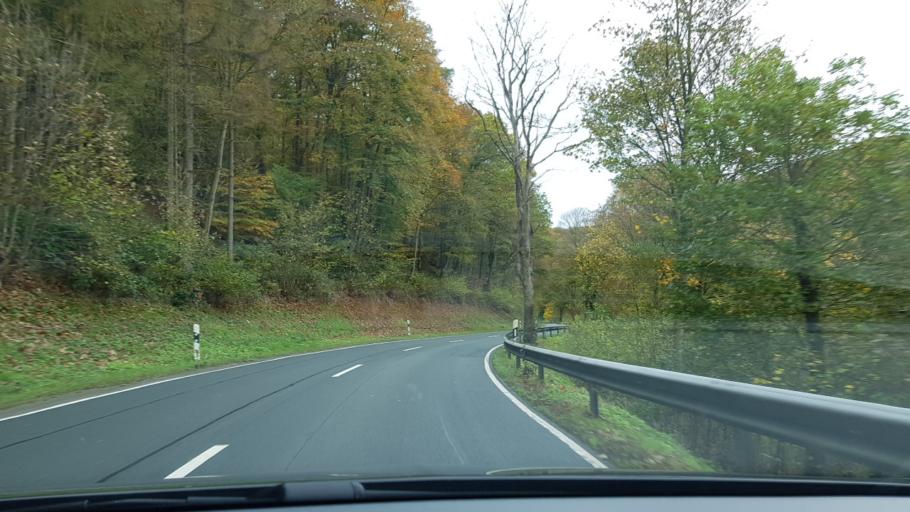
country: DE
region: Rheinland-Pfalz
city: Kalenborn
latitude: 50.5381
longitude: 7.0008
